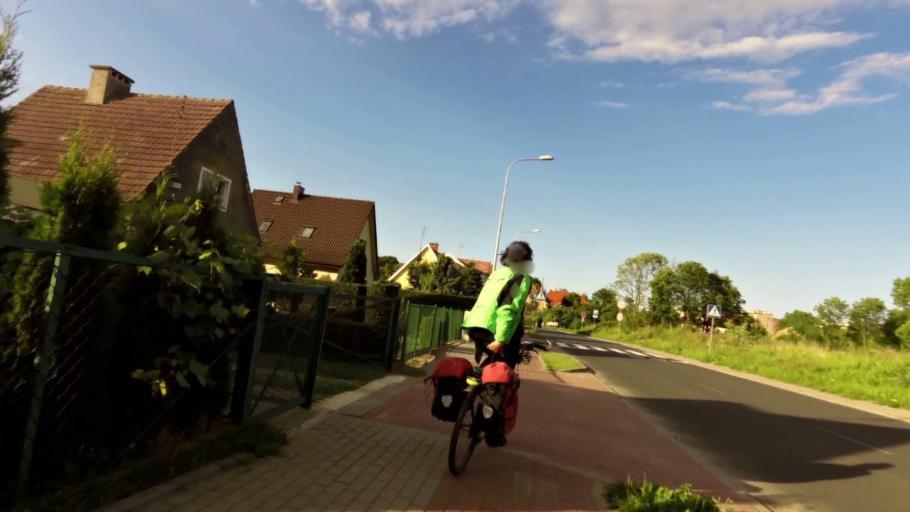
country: PL
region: West Pomeranian Voivodeship
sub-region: Powiat slawienski
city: Darlowo
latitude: 54.4159
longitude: 16.4032
